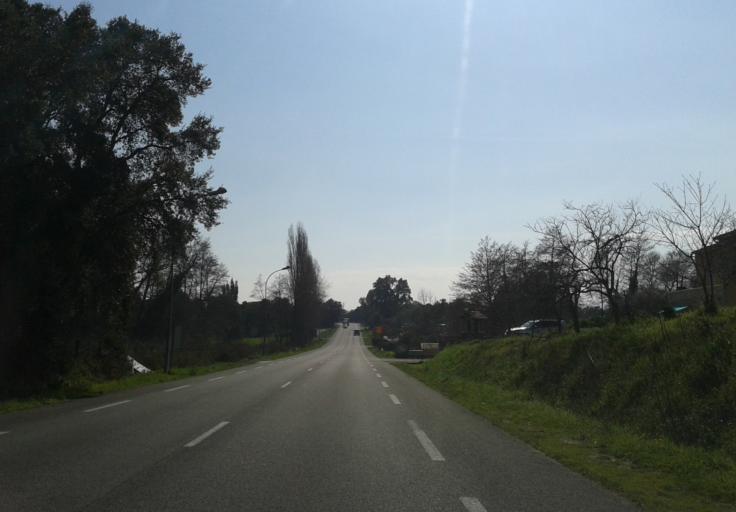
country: FR
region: Corsica
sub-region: Departement de la Haute-Corse
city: Linguizzetta
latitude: 42.2193
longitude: 9.5364
